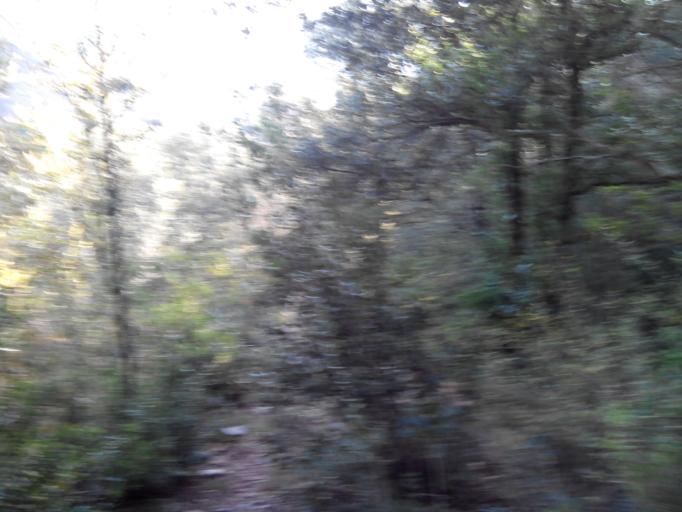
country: ES
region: Catalonia
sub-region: Provincia de Barcelona
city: Vilada
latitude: 42.1138
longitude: 1.9354
